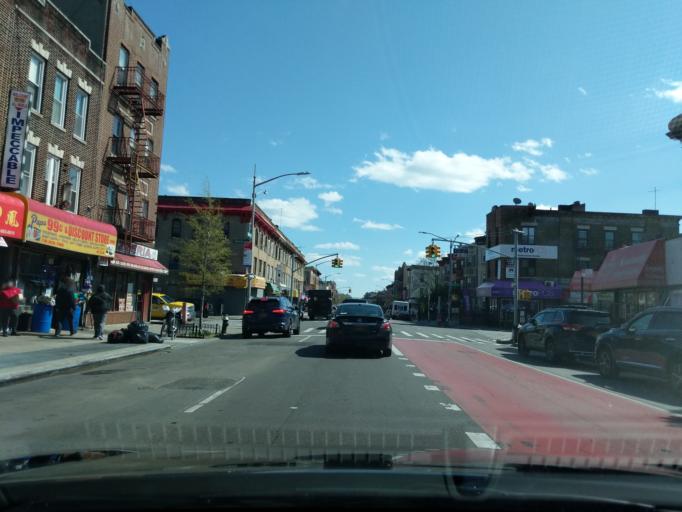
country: US
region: New York
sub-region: Kings County
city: Brooklyn
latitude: 40.6455
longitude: -73.9489
